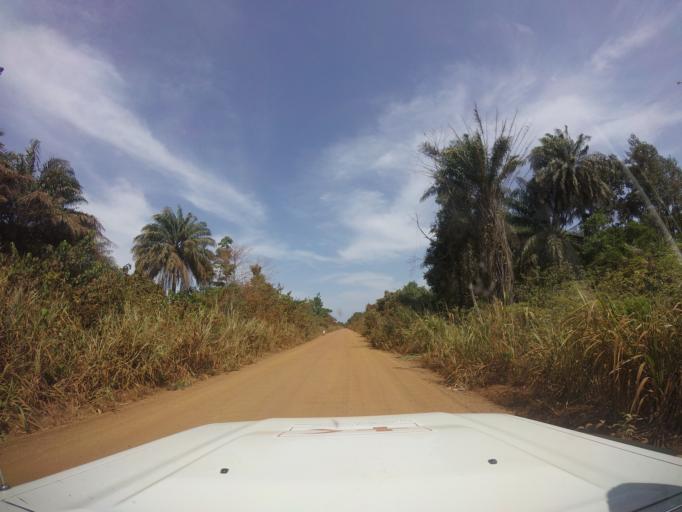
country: LR
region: Grand Cape Mount
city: Robertsport
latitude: 6.6841
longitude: -11.2429
